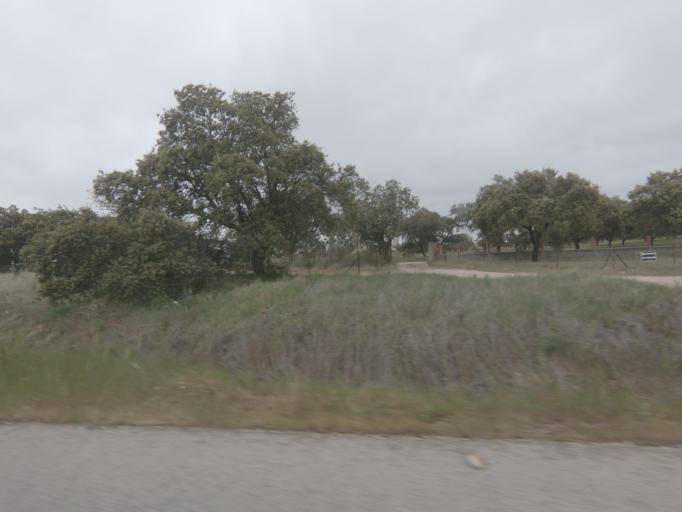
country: ES
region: Extremadura
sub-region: Provincia de Caceres
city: Caceres
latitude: 39.3977
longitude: -6.4234
